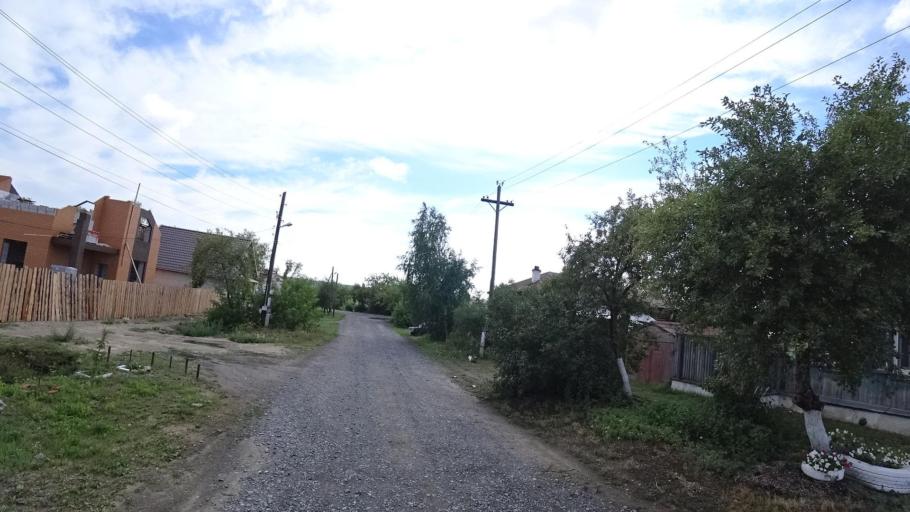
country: RU
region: Sverdlovsk
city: Kamyshlov
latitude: 56.8394
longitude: 62.7068
